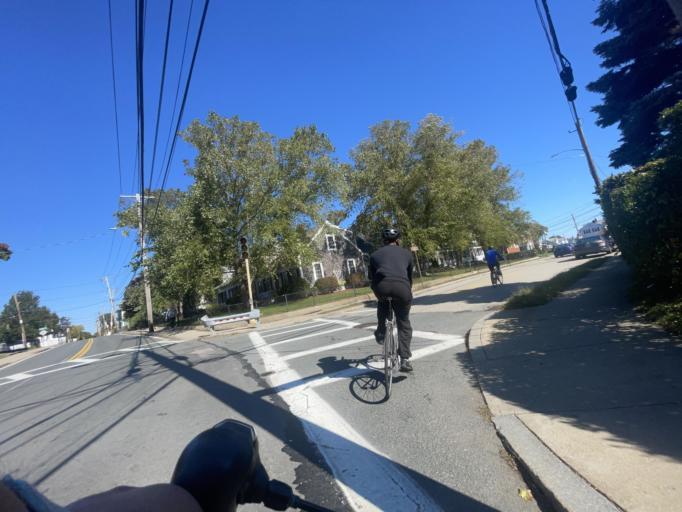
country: US
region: Massachusetts
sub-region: Norfolk County
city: Quincy
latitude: 42.2810
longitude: -71.0240
